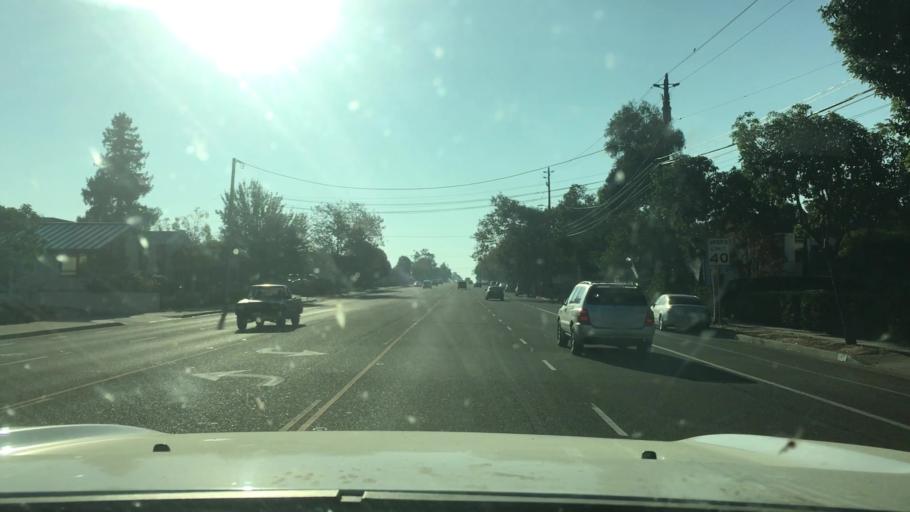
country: US
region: California
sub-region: San Luis Obispo County
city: San Luis Obispo
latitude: 35.2672
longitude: -120.6546
